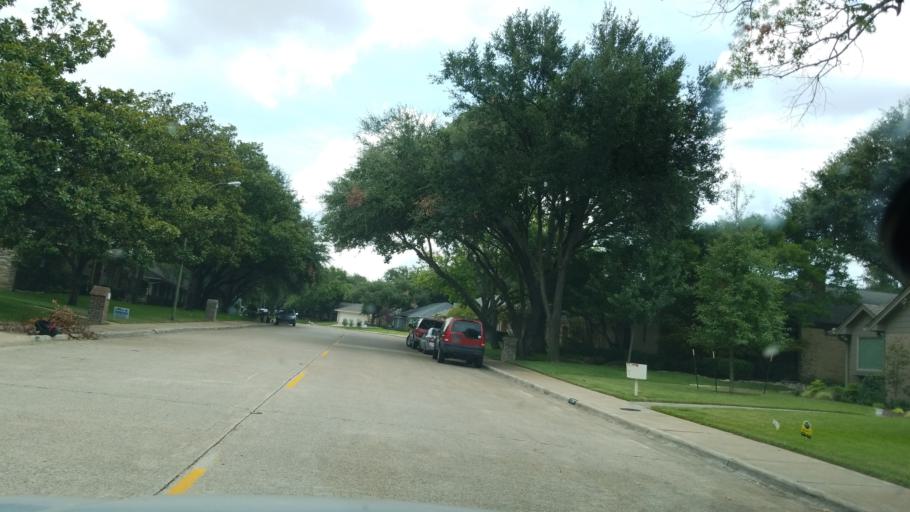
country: US
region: Texas
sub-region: Dallas County
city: Richardson
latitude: 32.8922
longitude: -96.7224
